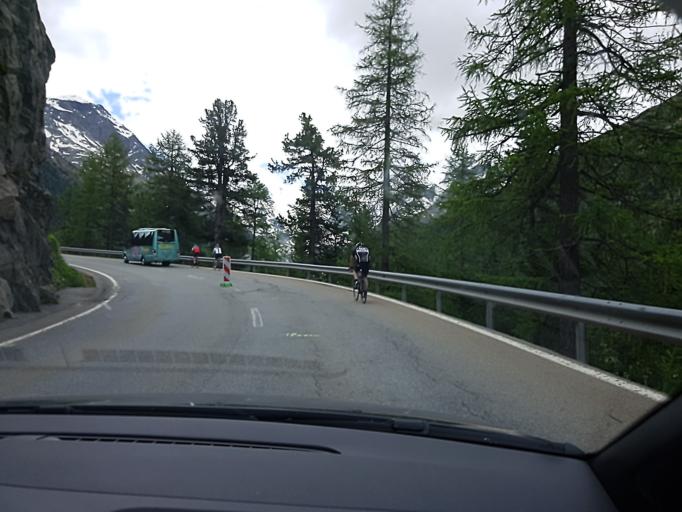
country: CH
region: Grisons
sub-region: Maloja District
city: Pontresina
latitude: 46.4579
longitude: 9.9413
